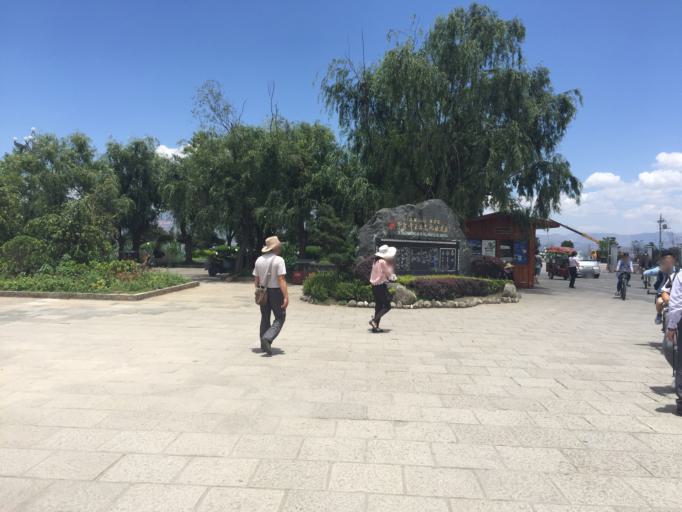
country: CN
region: Yunnan
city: Dali
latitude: 25.7087
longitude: 100.1497
